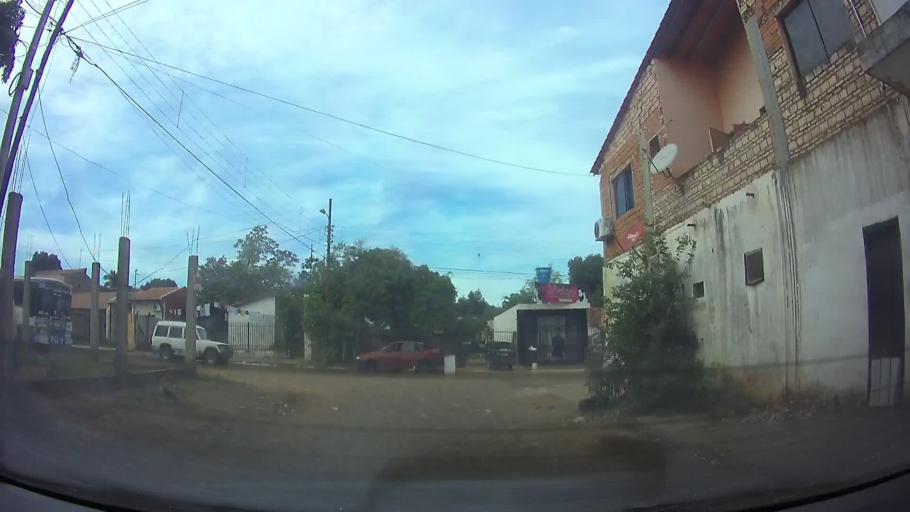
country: PY
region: Central
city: Fernando de la Mora
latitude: -25.3452
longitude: -57.5541
